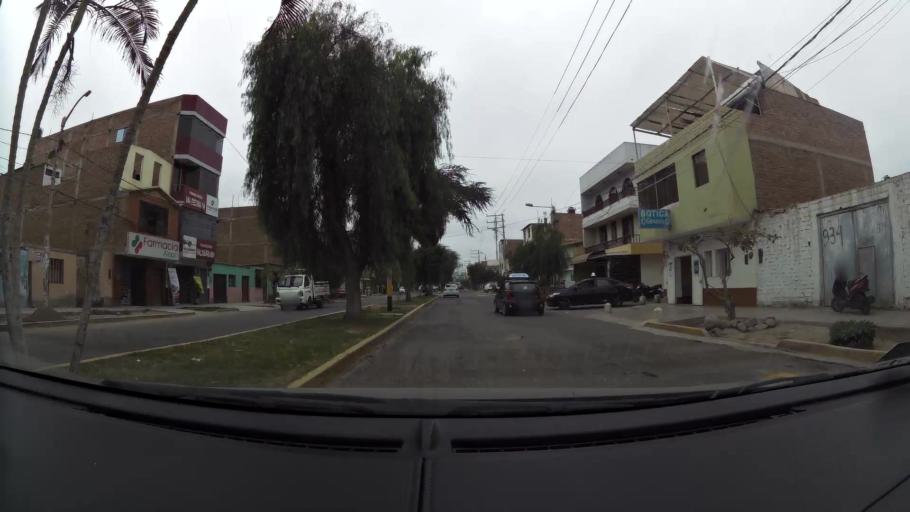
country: PE
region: La Libertad
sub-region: Provincia de Trujillo
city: Buenos Aires
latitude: -8.1389
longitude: -79.0453
